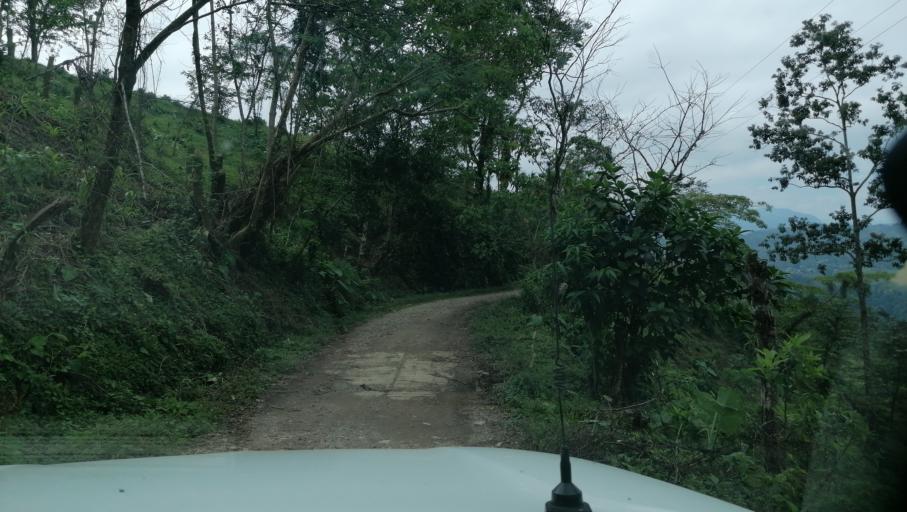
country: MX
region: Chiapas
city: Ixtacomitan
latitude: 17.3598
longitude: -93.1225
